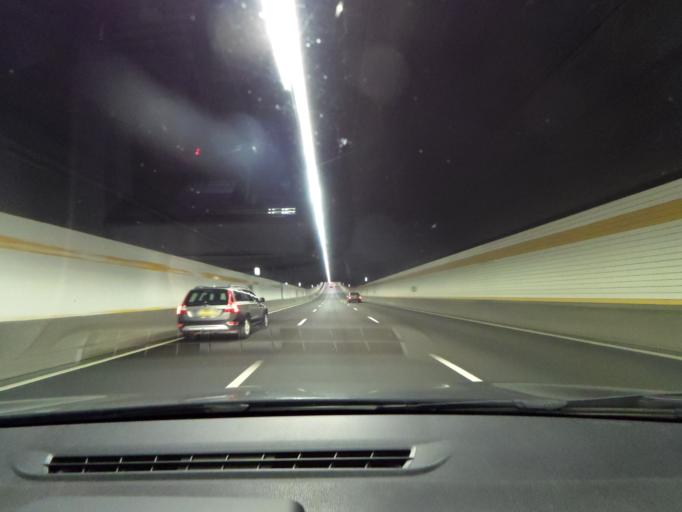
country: NL
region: South Holland
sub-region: Gemeente Barendrecht
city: Barendrecht
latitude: 51.8343
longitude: 4.5125
